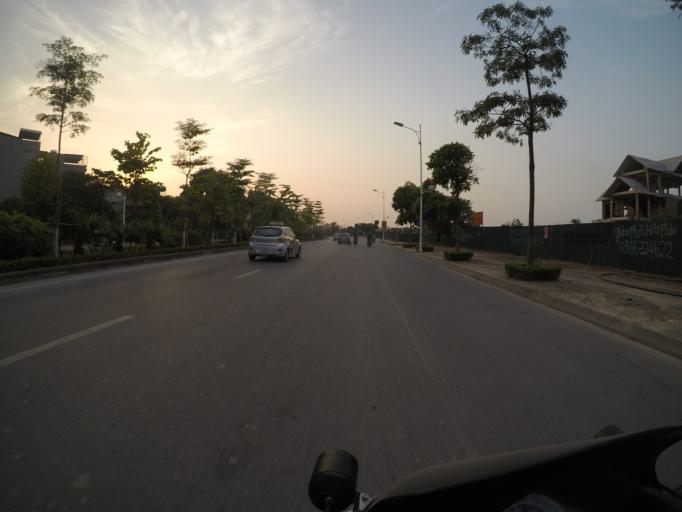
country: VN
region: Ha Noi
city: Hoan Kiem
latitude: 21.0295
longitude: 105.8849
